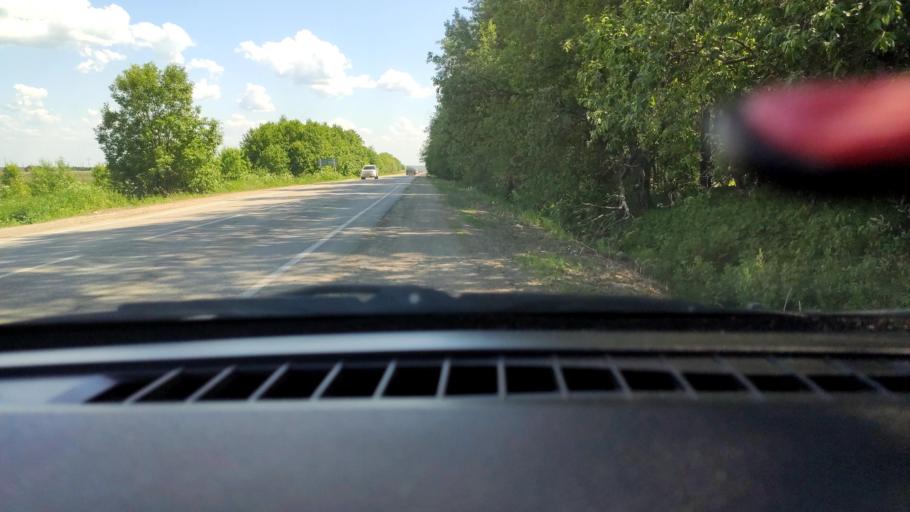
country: RU
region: Perm
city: Sylva
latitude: 58.0136
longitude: 56.7532
